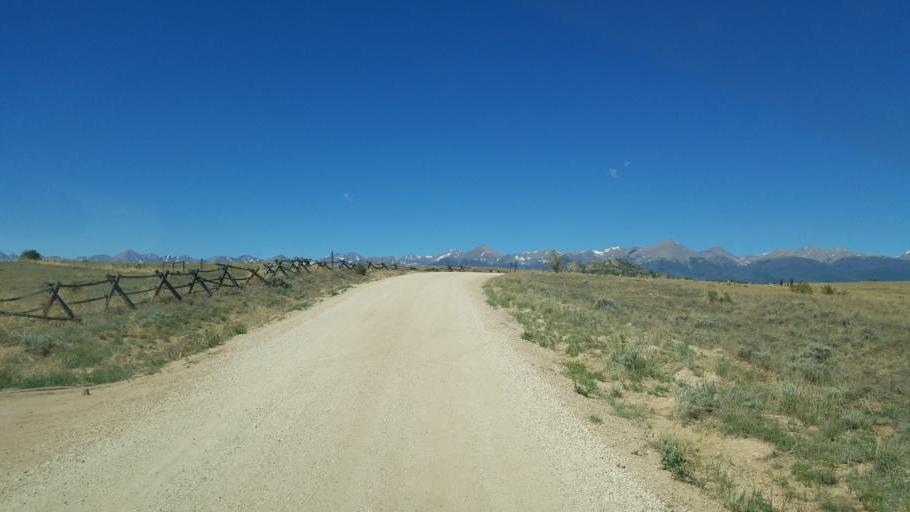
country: US
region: Colorado
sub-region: Custer County
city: Westcliffe
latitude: 38.2363
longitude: -105.4833
